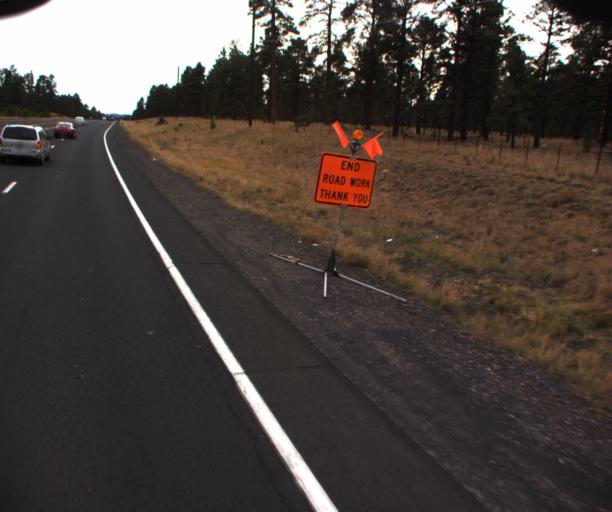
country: US
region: Arizona
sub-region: Coconino County
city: Flagstaff
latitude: 35.2830
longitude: -111.5423
